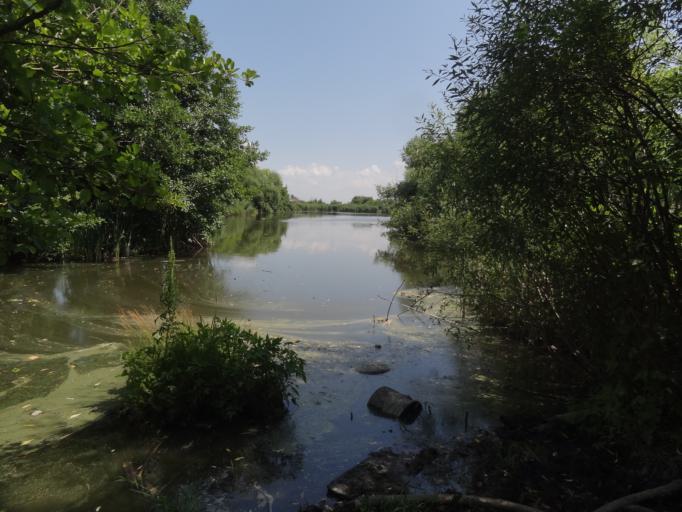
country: RU
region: Saratov
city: Sokolovyy
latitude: 51.4166
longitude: 45.8184
